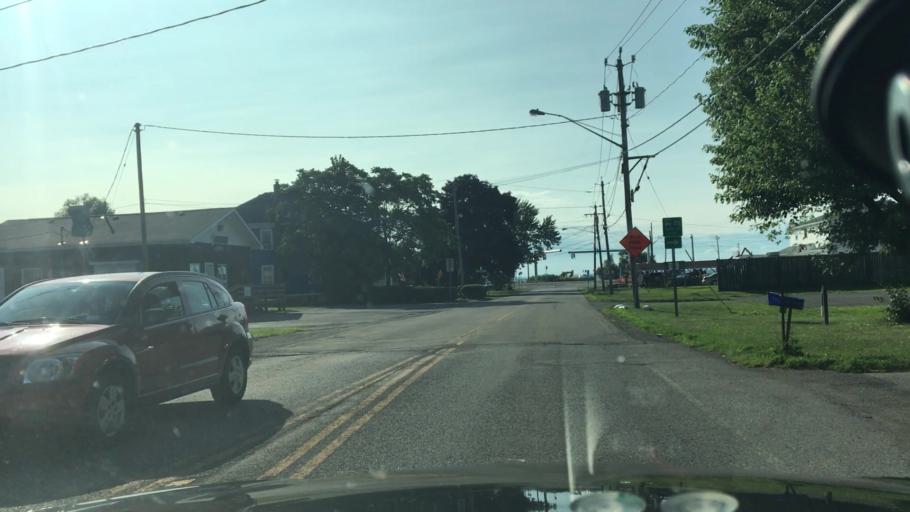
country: US
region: New York
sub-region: Erie County
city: Blasdell
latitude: 42.7728
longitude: -78.8616
